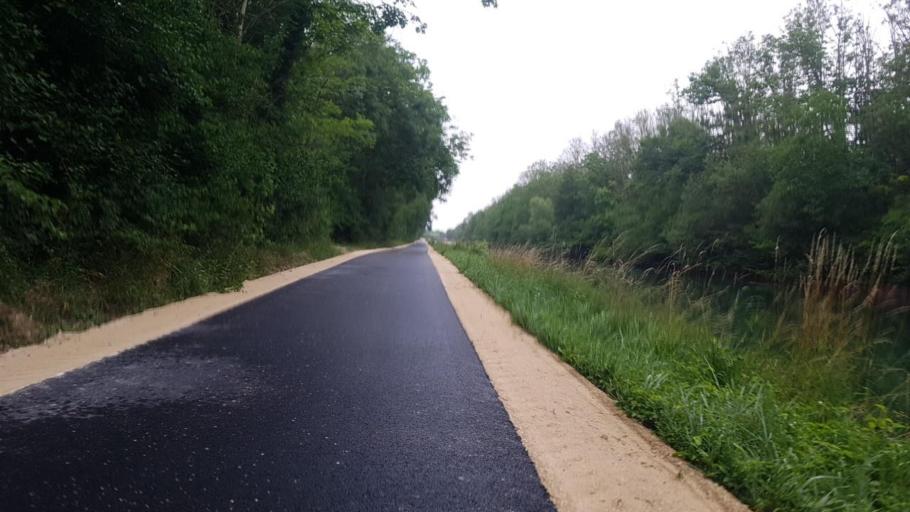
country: FR
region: Champagne-Ardenne
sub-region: Departement de la Marne
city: Vitry-le-Francois
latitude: 48.8025
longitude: 4.5231
